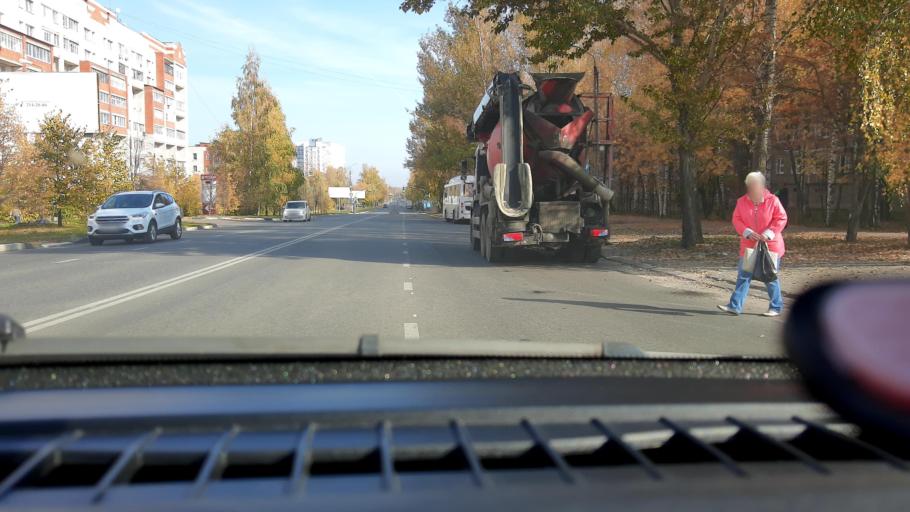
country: RU
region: Nizjnij Novgorod
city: Kstovo
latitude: 56.1473
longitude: 44.1802
